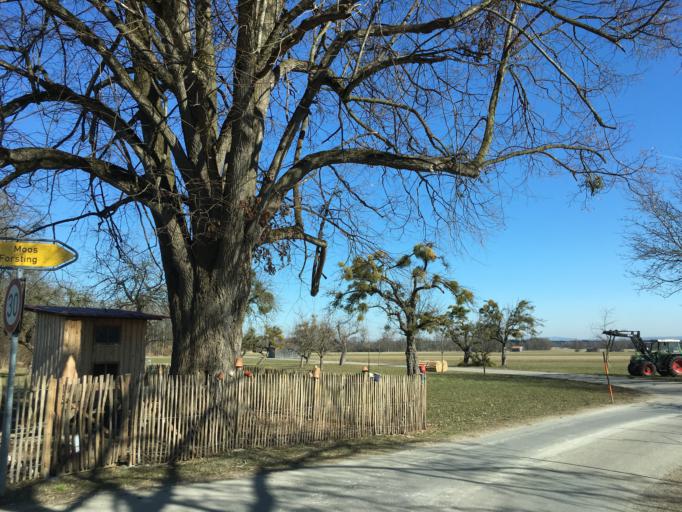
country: DE
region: Bavaria
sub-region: Upper Bavaria
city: Bad Aibling
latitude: 47.8244
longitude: 11.9771
